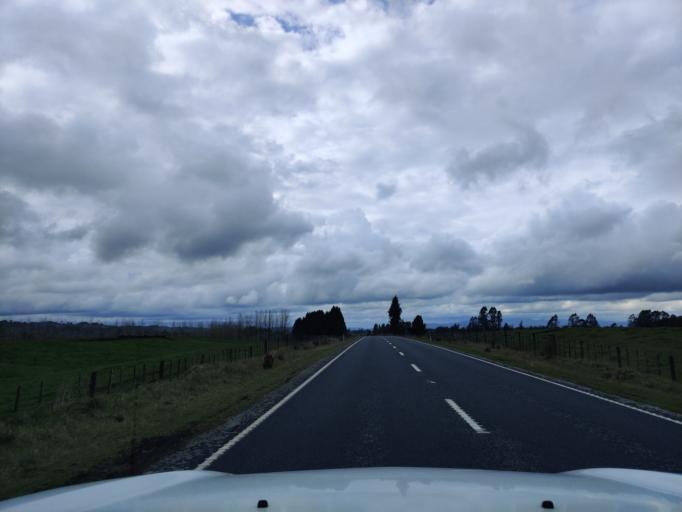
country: NZ
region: Waikato
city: Turangi
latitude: -39.0374
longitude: 175.3830
